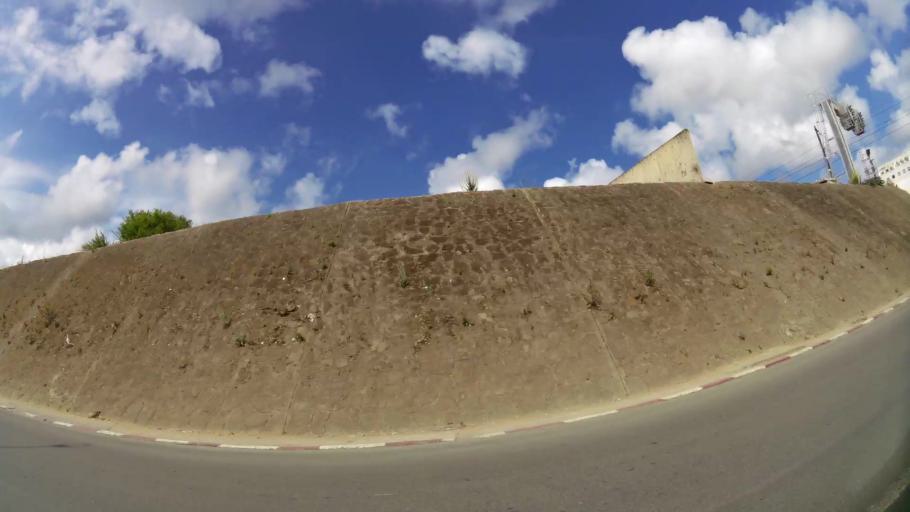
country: MA
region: Gharb-Chrarda-Beni Hssen
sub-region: Kenitra Province
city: Kenitra
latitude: 34.2541
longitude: -6.5742
